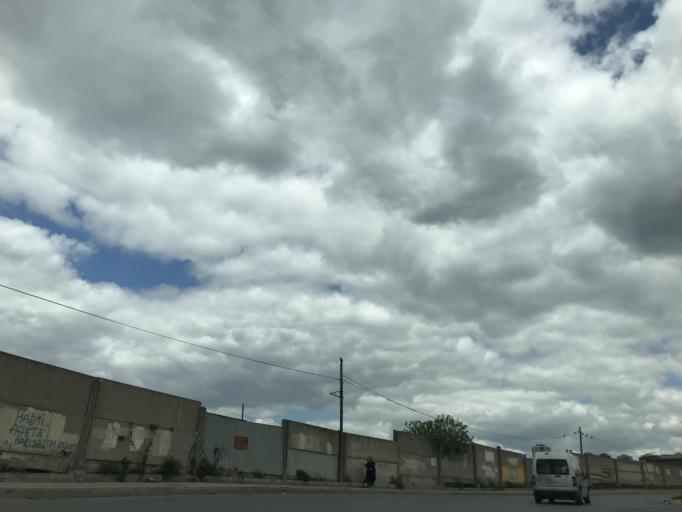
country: TR
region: Istanbul
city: Maltepe
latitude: 40.9022
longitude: 29.2073
